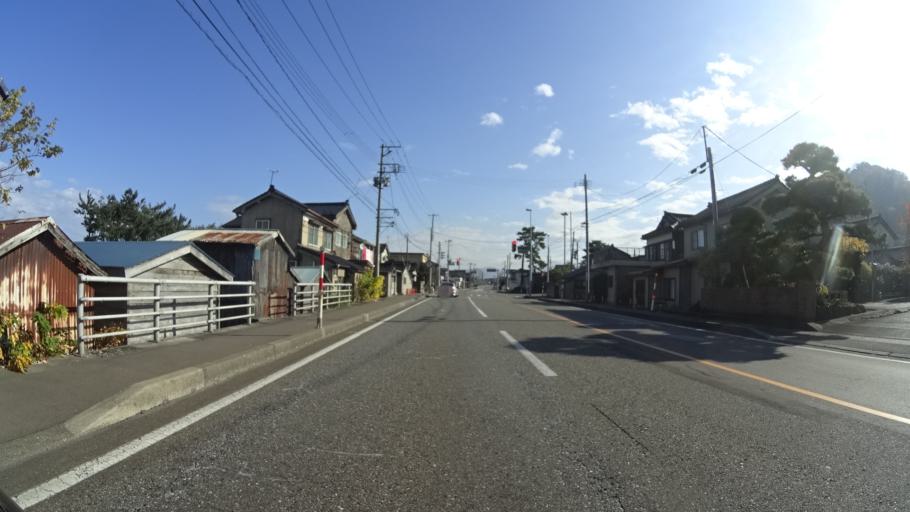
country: JP
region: Niigata
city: Itoigawa
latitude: 37.0252
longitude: 137.7981
